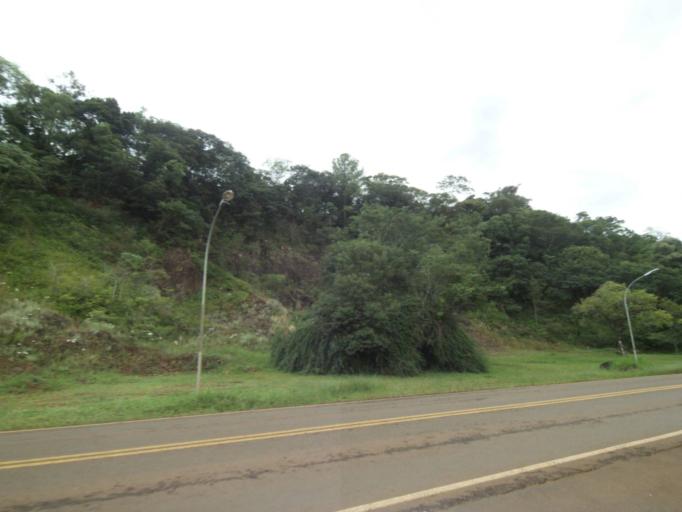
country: BR
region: Parana
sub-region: Guaraniacu
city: Guaraniacu
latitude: -25.1002
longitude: -52.8902
